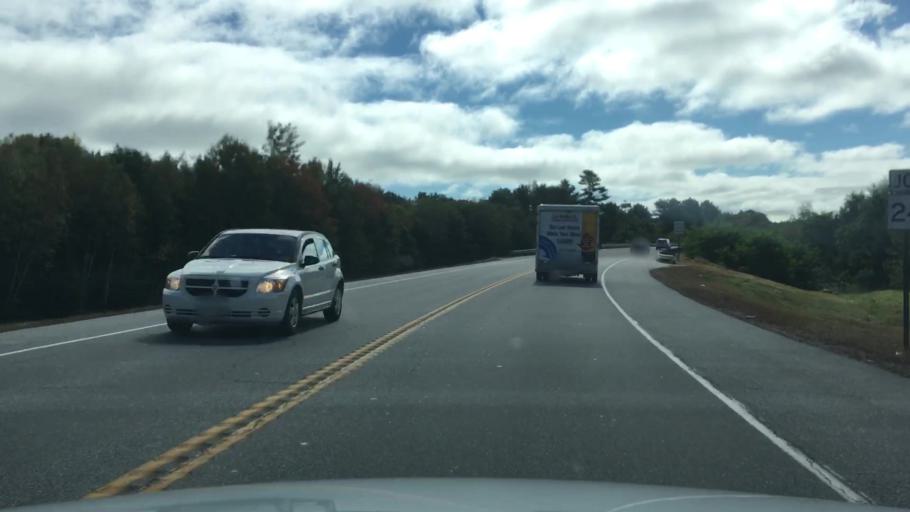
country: US
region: Maine
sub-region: Cumberland County
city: Brunswick
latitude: 43.9325
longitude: -69.9493
